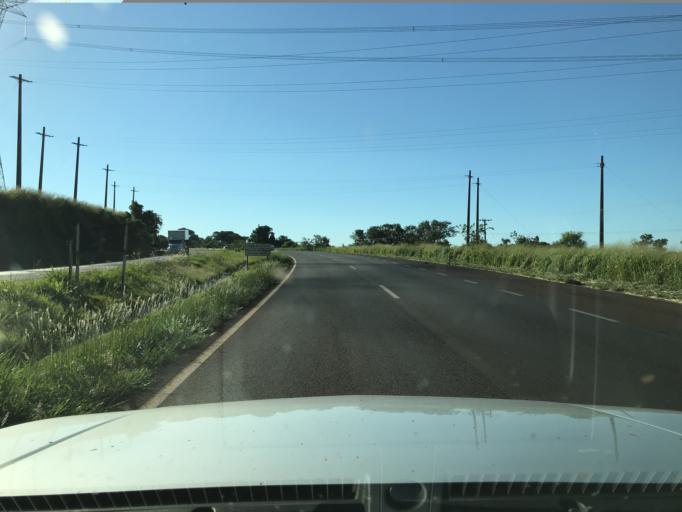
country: BR
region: Parana
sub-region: Cascavel
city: Cascavel
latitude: -24.8575
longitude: -53.5916
